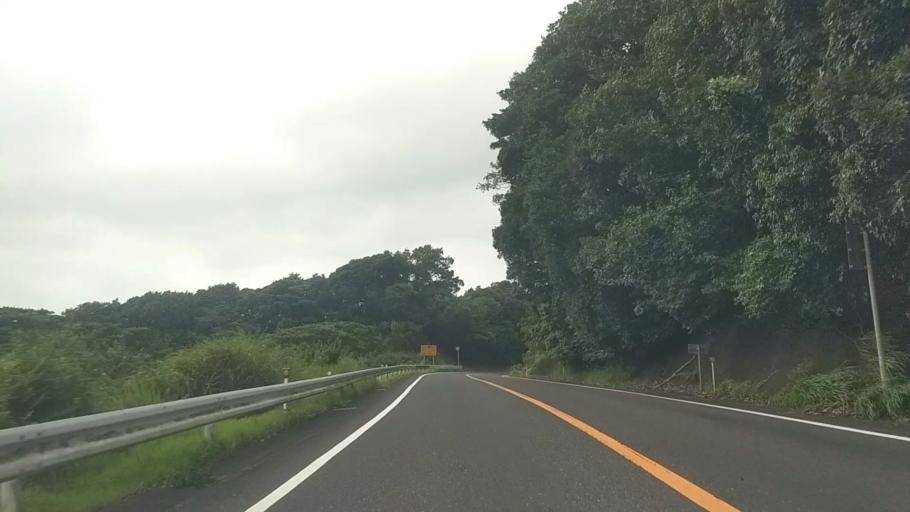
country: JP
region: Chiba
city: Kawaguchi
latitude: 35.2112
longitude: 140.0530
